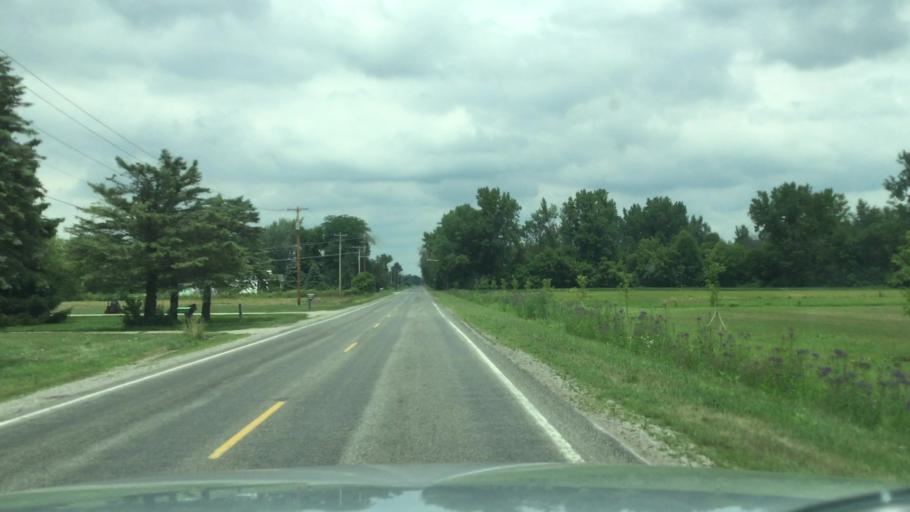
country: US
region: Michigan
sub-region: Saginaw County
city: Burt
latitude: 43.2852
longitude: -83.8944
